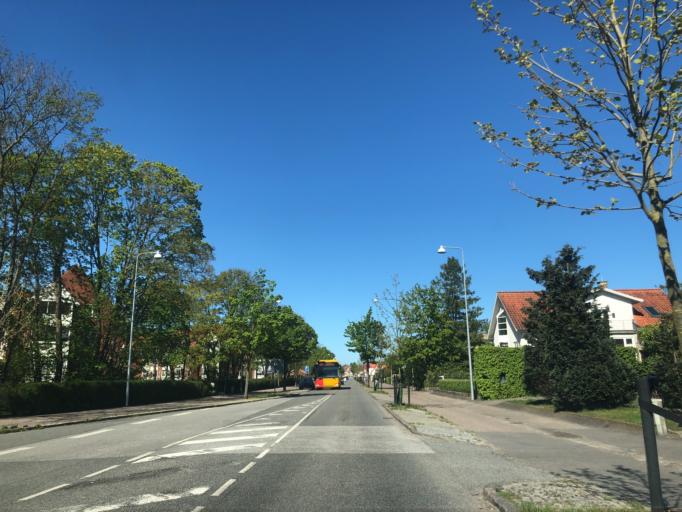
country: DK
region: Zealand
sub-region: Koge Kommune
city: Koge
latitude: 55.4499
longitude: 12.1763
